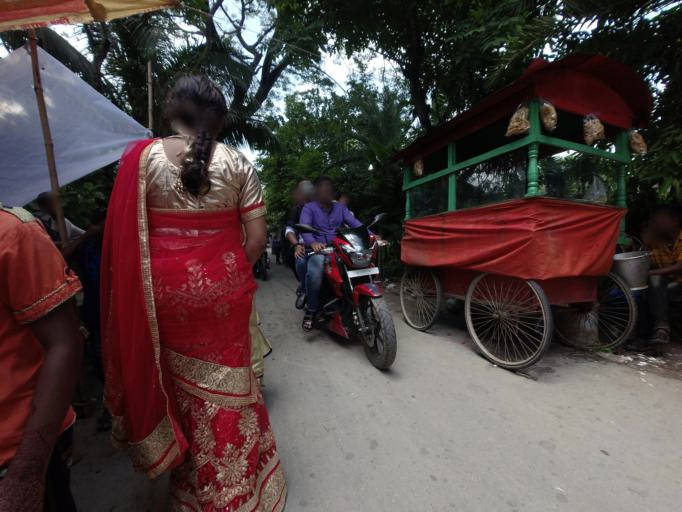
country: BD
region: Khulna
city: Kalia
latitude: 23.0368
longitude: 89.6283
